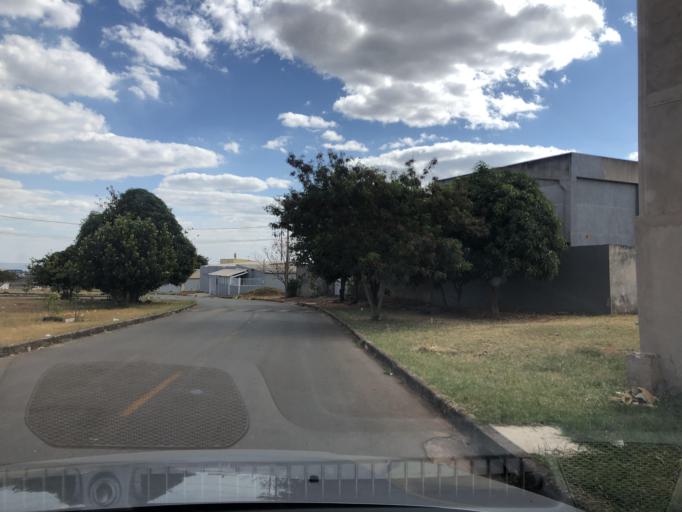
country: BR
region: Federal District
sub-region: Brasilia
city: Brasilia
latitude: -15.8824
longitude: -48.1248
